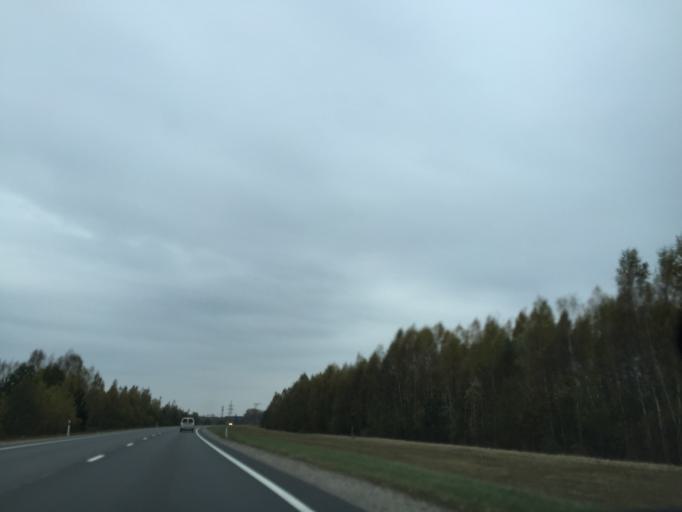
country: LV
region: Ozolnieku
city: Ozolnieki
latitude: 56.6757
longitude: 23.8235
